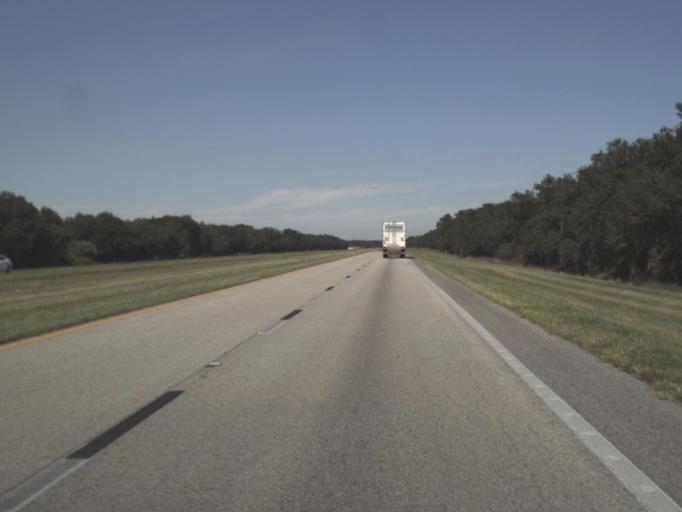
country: US
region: Florida
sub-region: Hendry County
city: Port LaBelle
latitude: 26.9590
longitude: -81.3164
